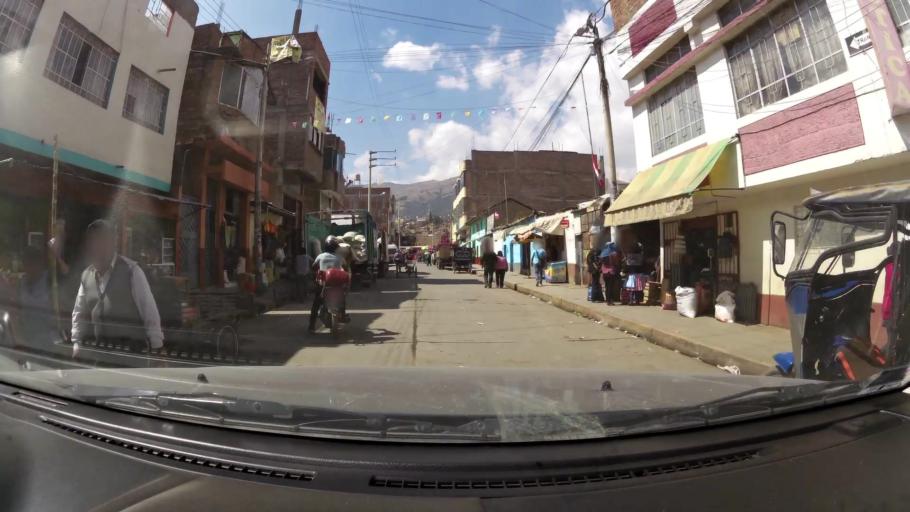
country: PE
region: Junin
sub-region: Provincia de Huancayo
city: Huancayo
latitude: -12.0673
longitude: -75.2019
